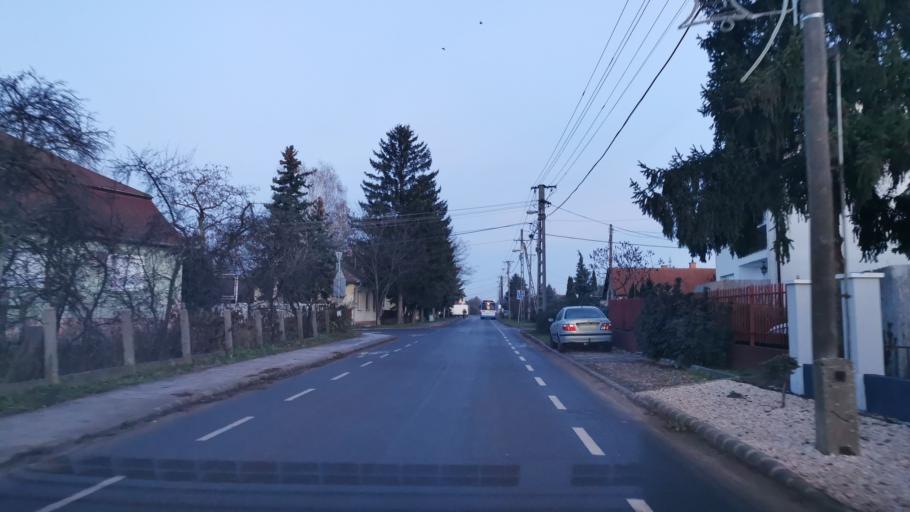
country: HU
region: Hajdu-Bihar
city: Hajduboszormeny
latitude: 47.5925
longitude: 21.5639
